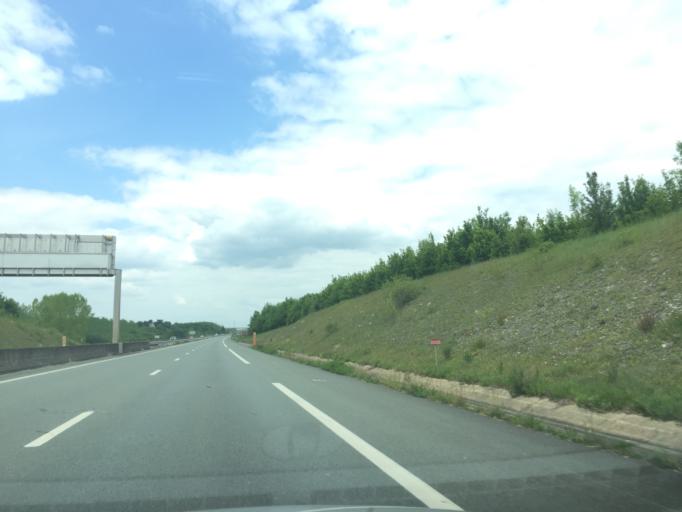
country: FR
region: Poitou-Charentes
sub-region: Departement des Deux-Sevres
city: Chauray
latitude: 46.3707
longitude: -0.3551
